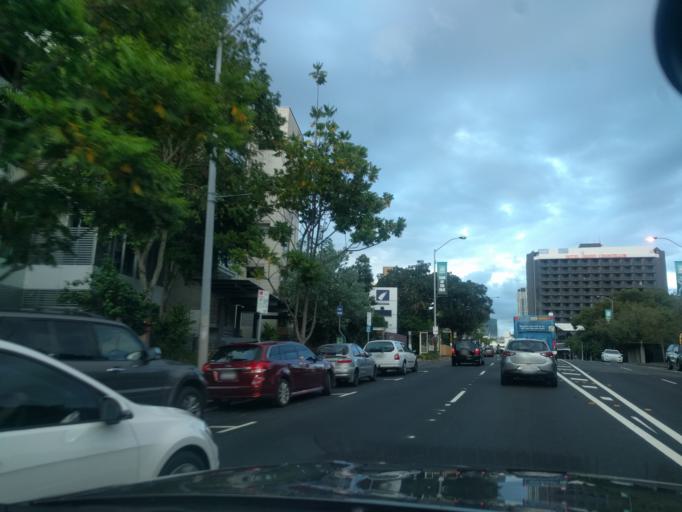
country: AU
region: Queensland
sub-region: Brisbane
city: Spring Hill
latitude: -27.4615
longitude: 153.0198
